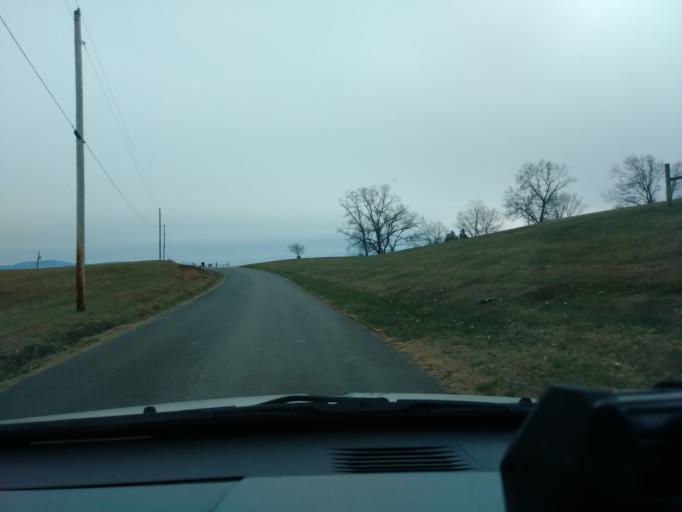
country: US
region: Tennessee
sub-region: Greene County
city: Greeneville
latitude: 36.0868
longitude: -82.8916
